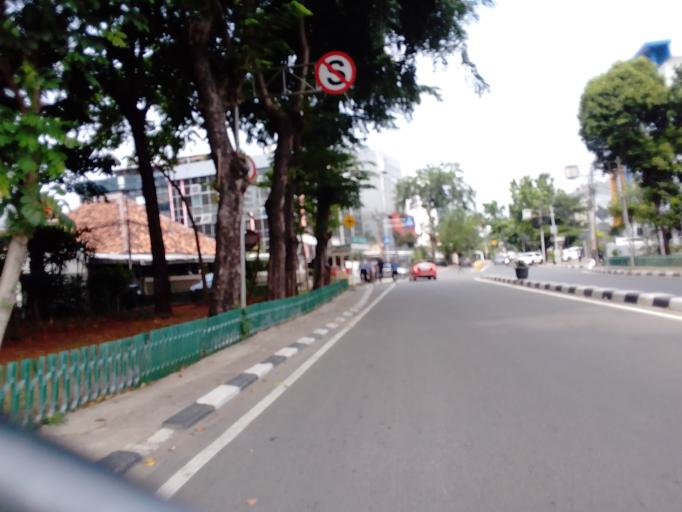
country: ID
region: Jakarta Raya
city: Jakarta
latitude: -6.1724
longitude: 106.8089
